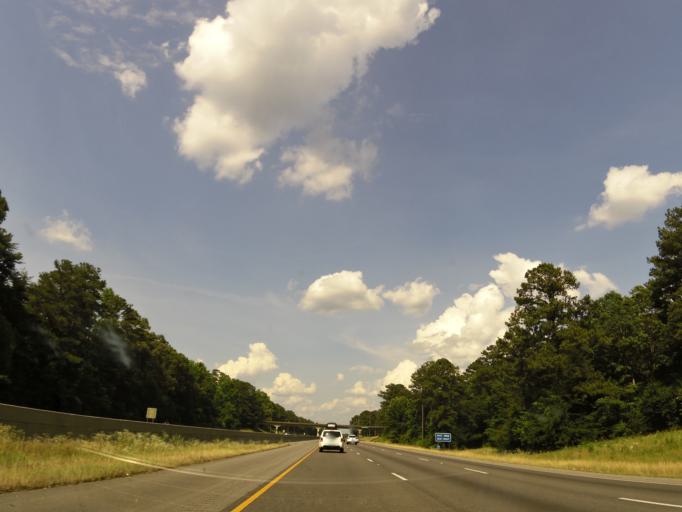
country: US
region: Alabama
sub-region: Tuscaloosa County
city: Coaling
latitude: 33.1872
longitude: -87.3313
